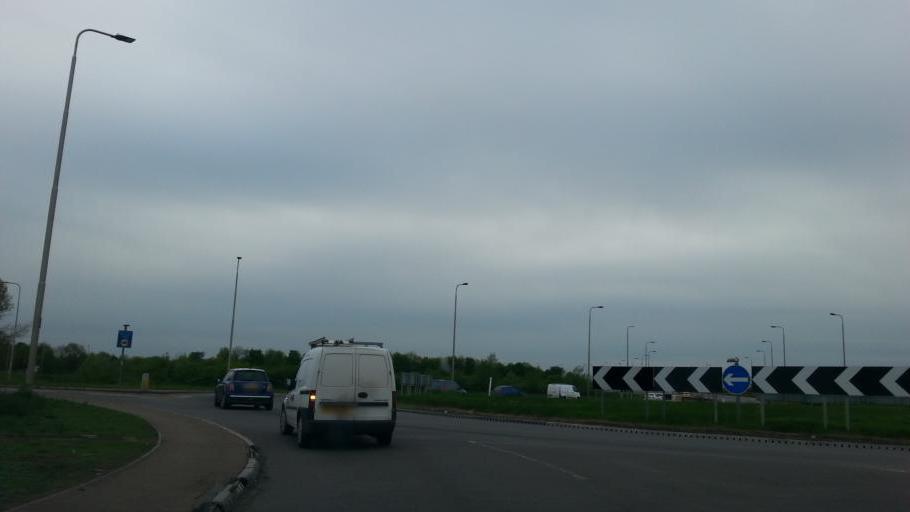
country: GB
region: England
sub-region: Peterborough
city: Eye
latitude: 52.6059
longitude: -0.2216
